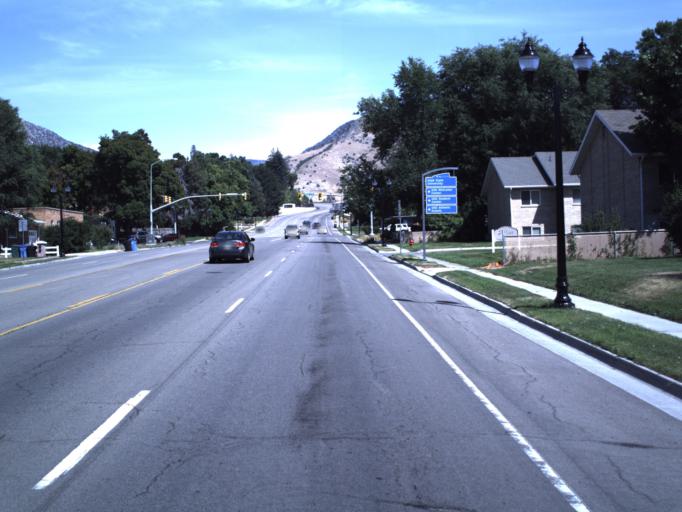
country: US
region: Utah
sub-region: Cache County
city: Logan
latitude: 41.7388
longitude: -111.8211
